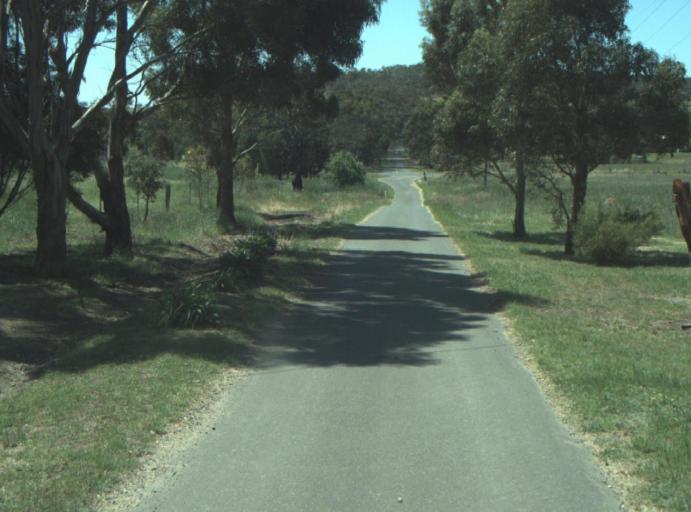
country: AU
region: Victoria
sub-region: Greater Geelong
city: Lara
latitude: -37.8728
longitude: 144.2708
